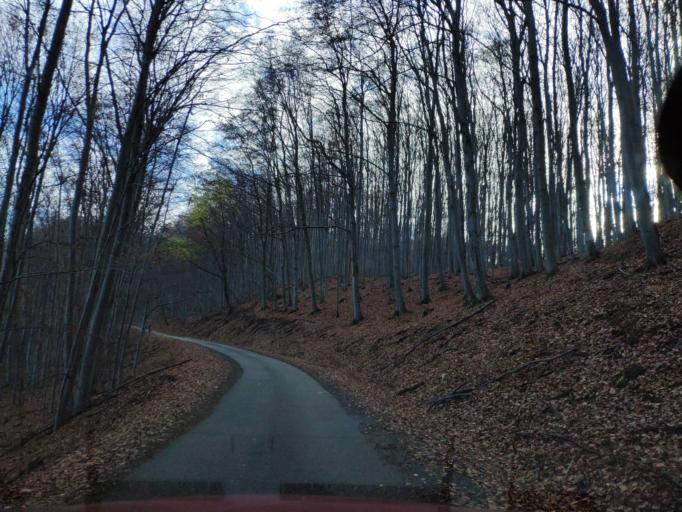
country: HU
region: Borsod-Abauj-Zemplen
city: Gonc
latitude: 48.5908
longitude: 21.4601
